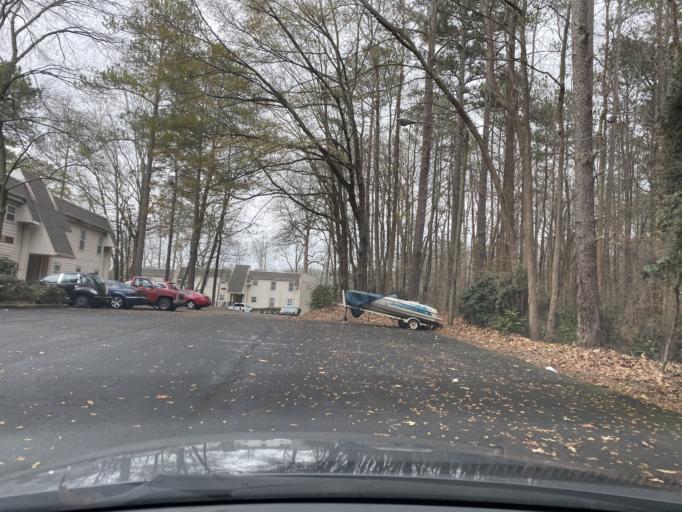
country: US
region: Georgia
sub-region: DeKalb County
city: Pine Mountain
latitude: 33.6948
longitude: -84.1449
